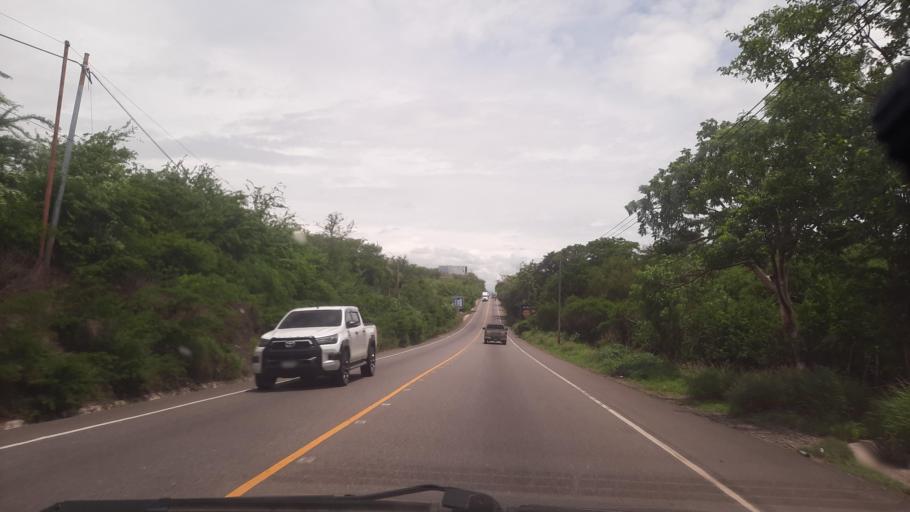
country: GT
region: Zacapa
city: Rio Hondo
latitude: 15.0474
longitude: -89.5700
